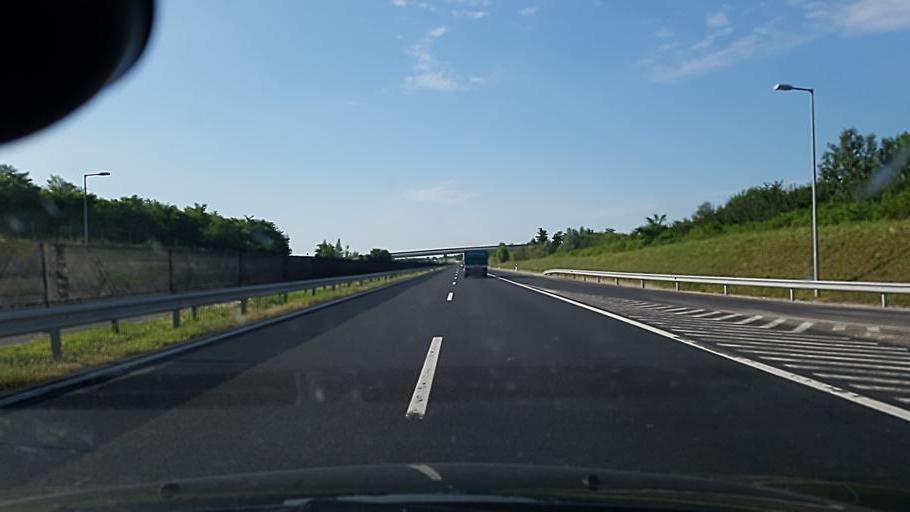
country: HU
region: Fejer
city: Adony
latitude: 47.0696
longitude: 18.8801
